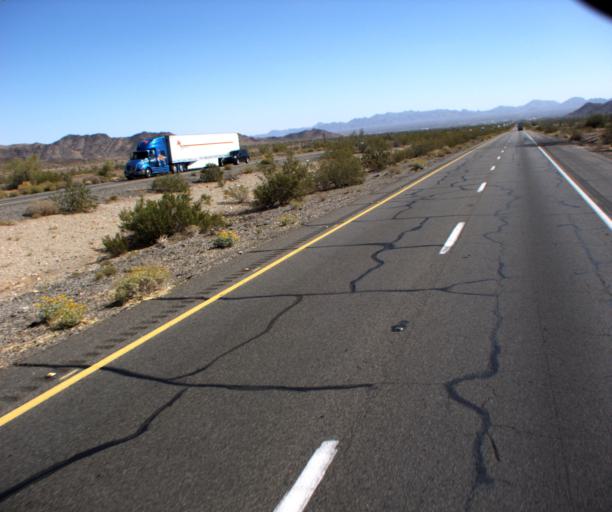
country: US
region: Arizona
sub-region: La Paz County
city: Quartzsite
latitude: 33.6501
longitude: -114.3074
